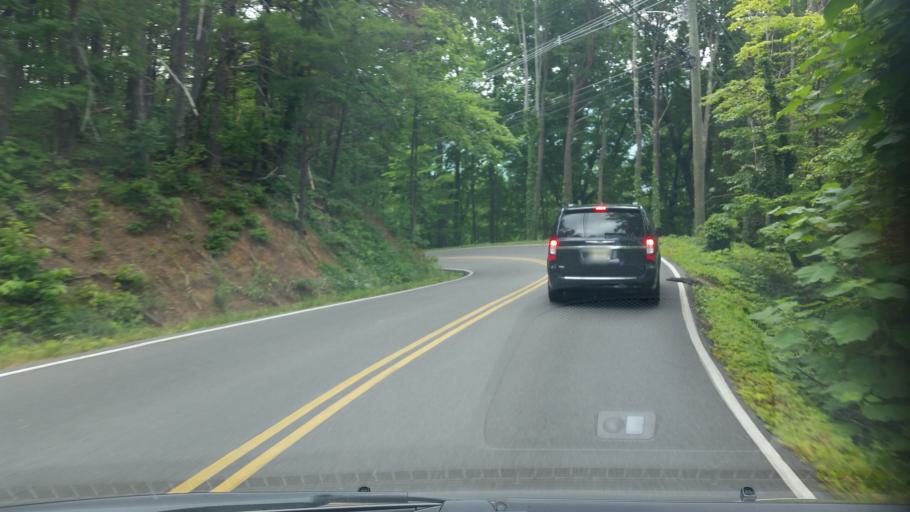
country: US
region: Tennessee
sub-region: Sevier County
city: Gatlinburg
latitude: 35.7119
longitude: -83.5424
